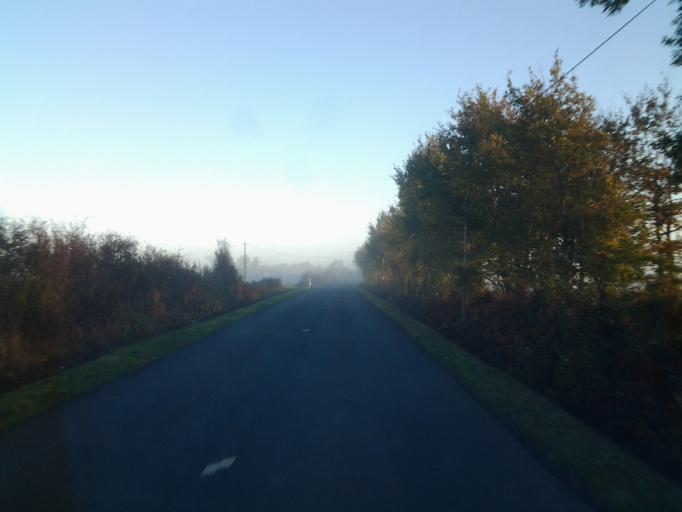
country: FR
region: Pays de la Loire
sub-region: Departement de la Vendee
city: Bournezeau
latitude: 46.6429
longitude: -1.2320
